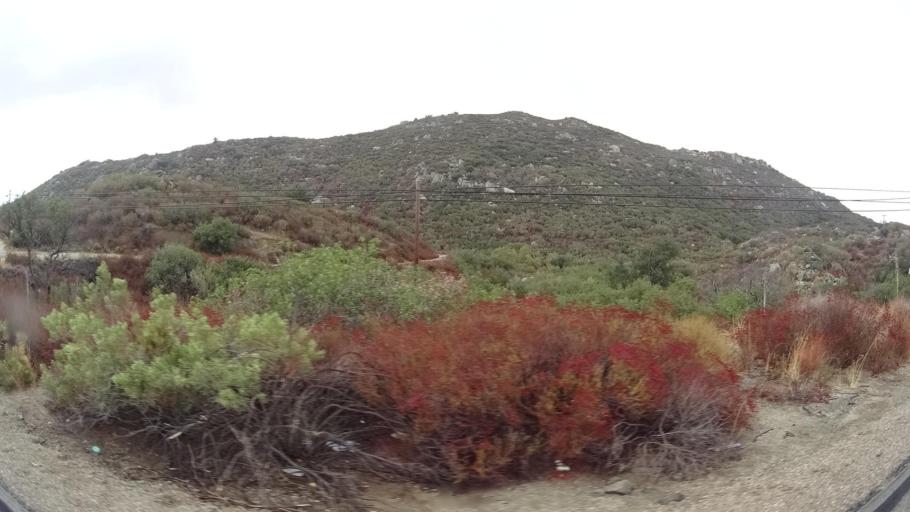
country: MX
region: Baja California
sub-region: Tecate
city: Hacienda Tecate
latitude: 32.5996
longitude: -116.5740
